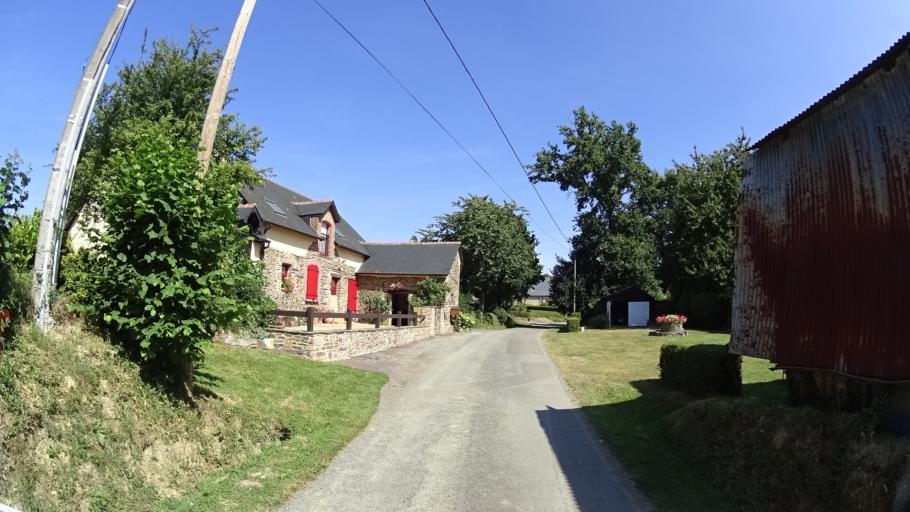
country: FR
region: Brittany
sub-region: Departement d'Ille-et-Vilaine
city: Orgeres
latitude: 47.9806
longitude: -1.6461
